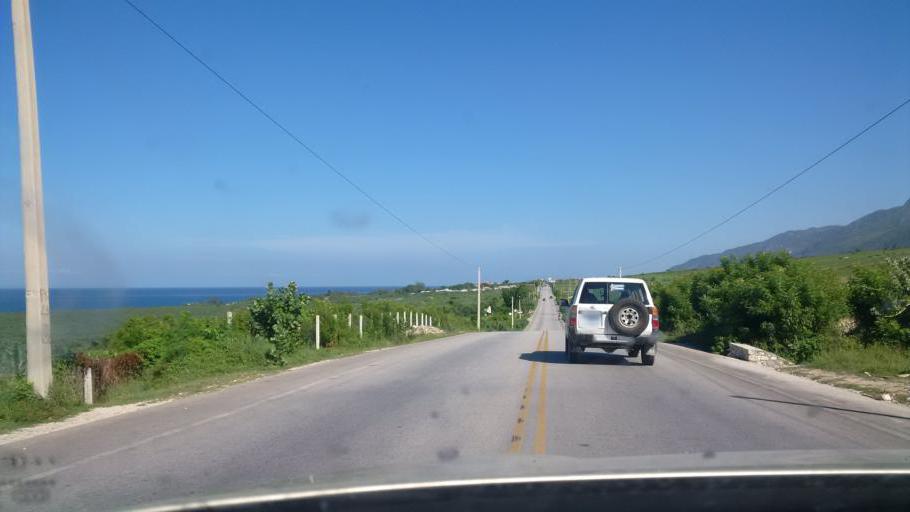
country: HT
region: Ouest
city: Cabaret
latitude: 18.8617
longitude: -72.5979
